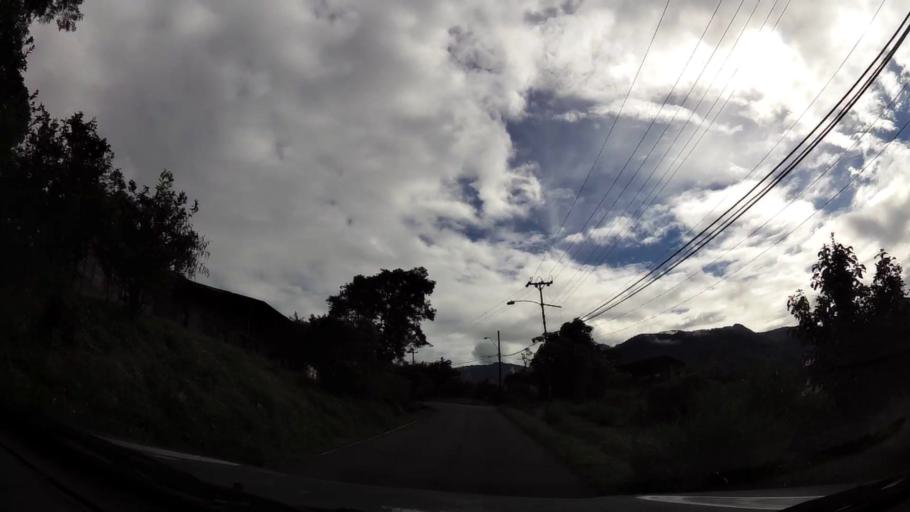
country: PA
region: Chiriqui
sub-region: Distrito Boquete
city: Boquete
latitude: 8.7981
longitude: -82.4372
